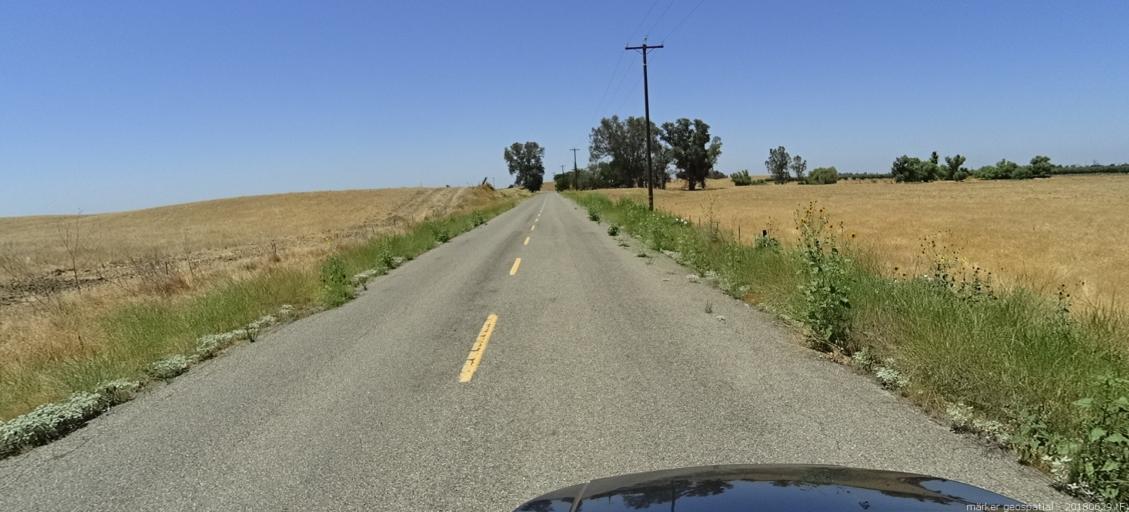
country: US
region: California
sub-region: Madera County
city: Bonadelle Ranchos-Madera Ranchos
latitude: 37.0211
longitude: -119.9558
